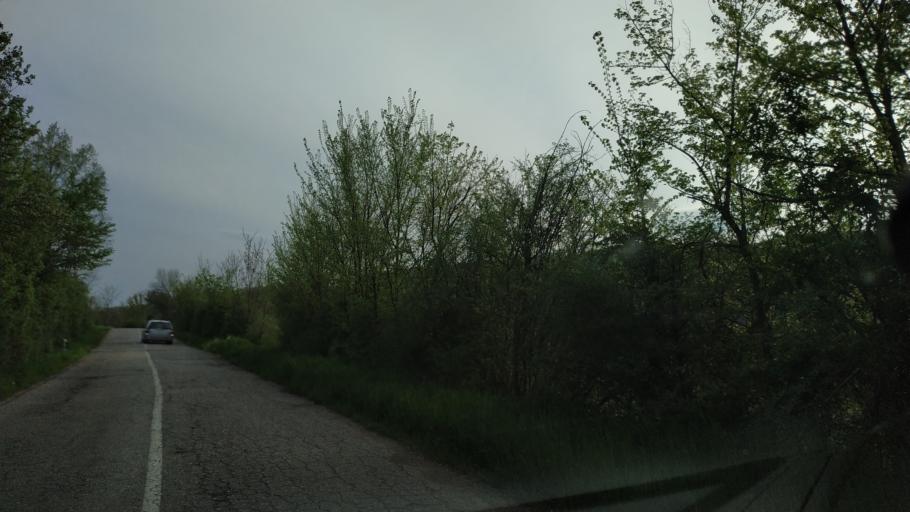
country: RS
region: Central Serbia
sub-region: Nisavski Okrug
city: Aleksinac
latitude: 43.4802
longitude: 21.8118
